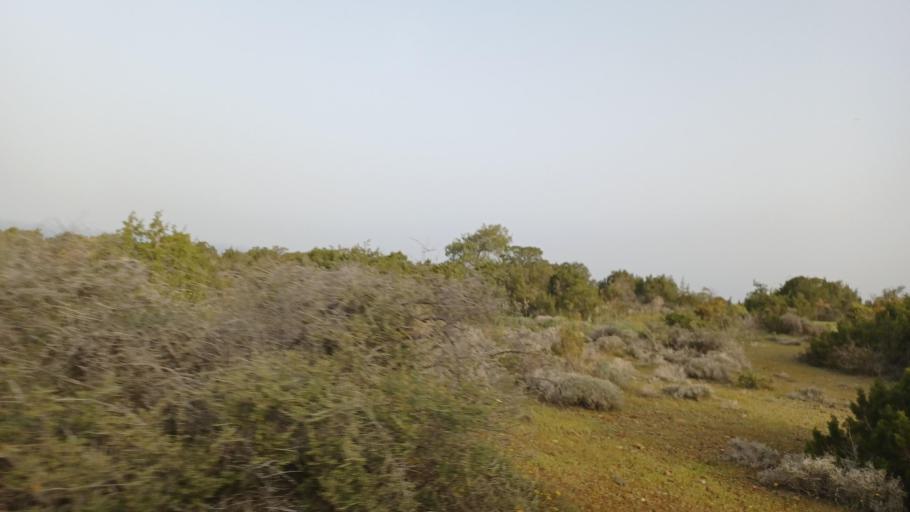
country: CY
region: Pafos
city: Pegeia
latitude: 34.9686
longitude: 32.3161
